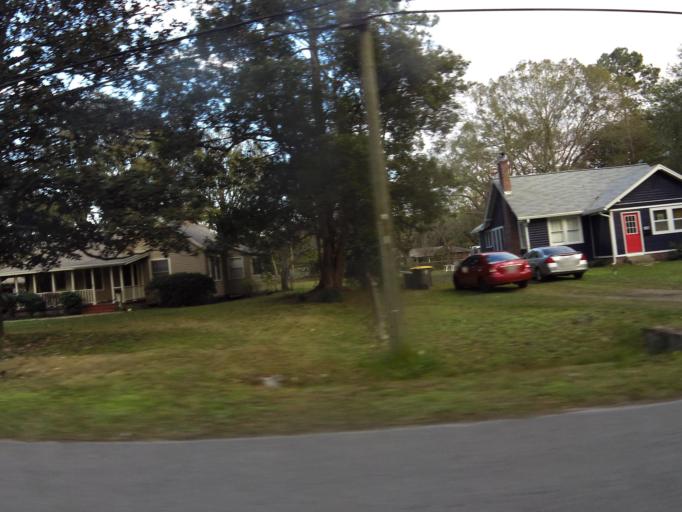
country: US
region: Florida
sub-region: Duval County
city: Jacksonville
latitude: 30.2986
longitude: -81.7262
